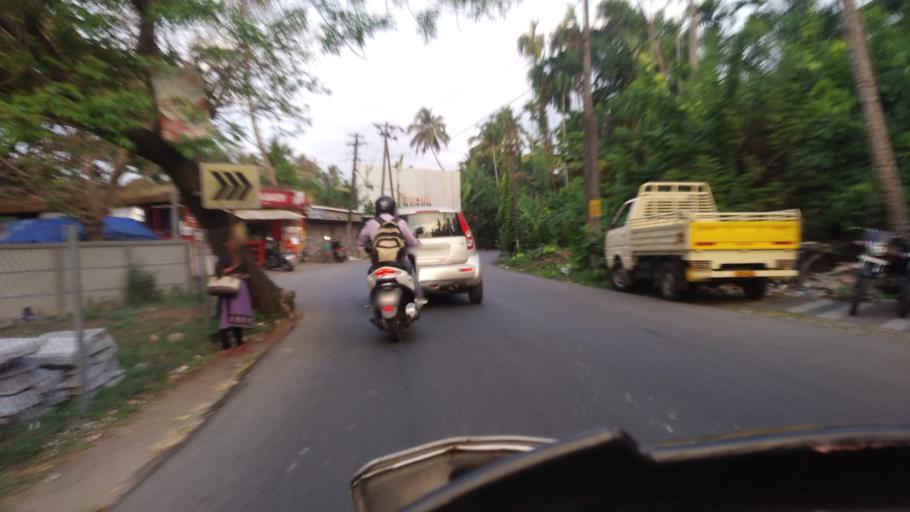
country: IN
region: Kerala
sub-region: Thrissur District
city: Kodungallur
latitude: 10.1869
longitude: 76.2029
